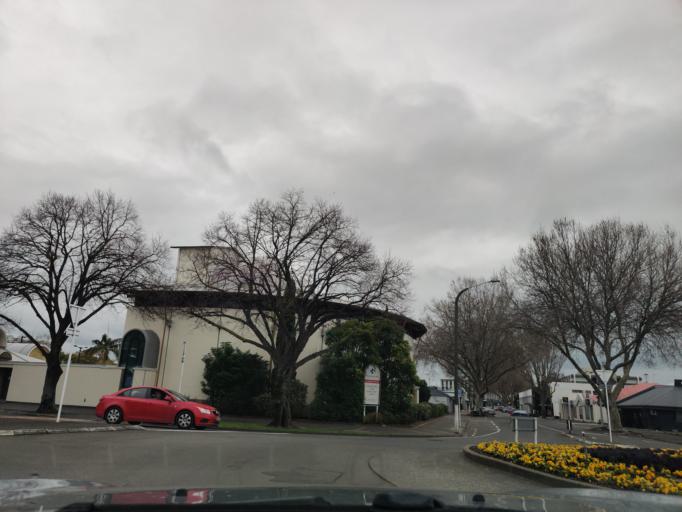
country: NZ
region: Hawke's Bay
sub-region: Napier City
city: Napier
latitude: -39.4932
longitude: 176.9140
